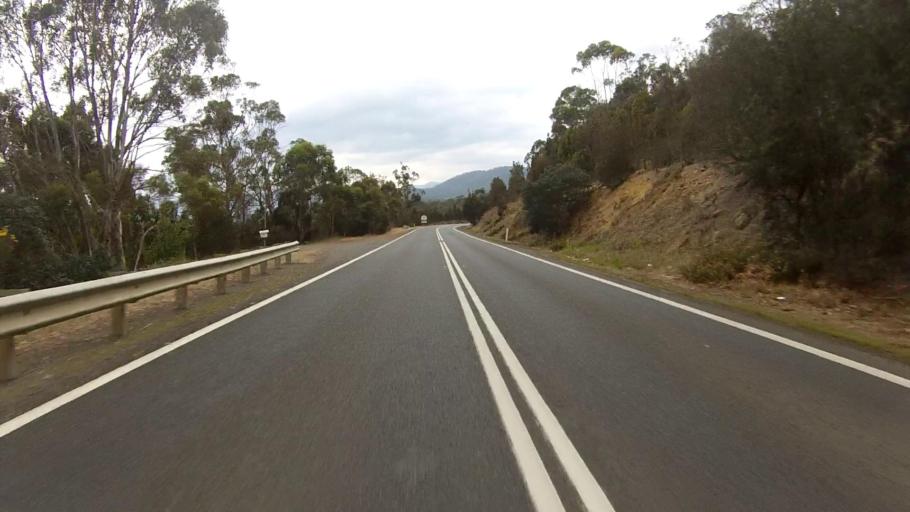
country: AU
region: Tasmania
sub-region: Huon Valley
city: Huonville
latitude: -43.0430
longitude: 147.0524
